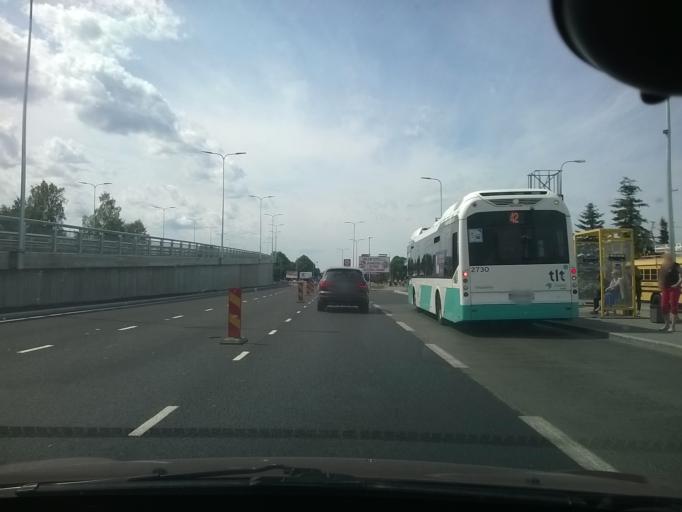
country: EE
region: Harju
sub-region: Saue vald
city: Laagri
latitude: 59.4247
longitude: 24.6506
